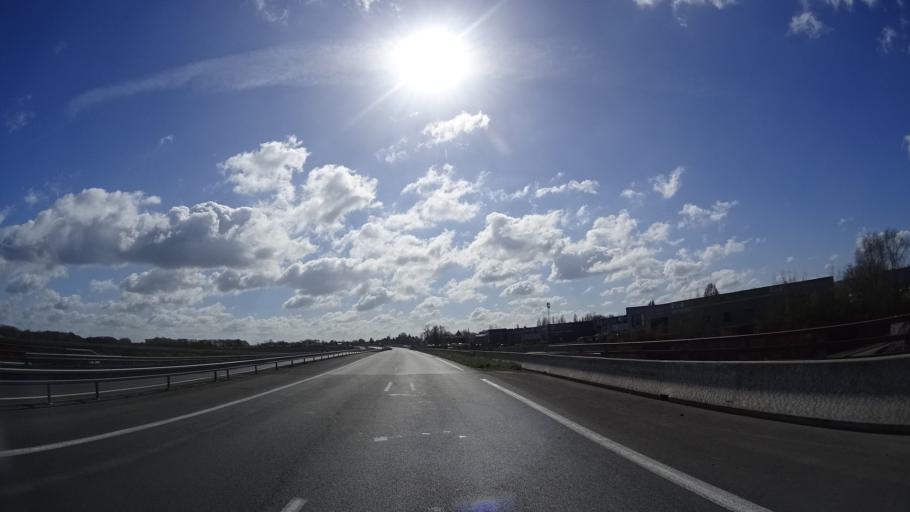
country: FR
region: Pays de la Loire
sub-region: Departement de Maine-et-Loire
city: Saint-Melaine-sur-Aubance
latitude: 47.3927
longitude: -0.5032
